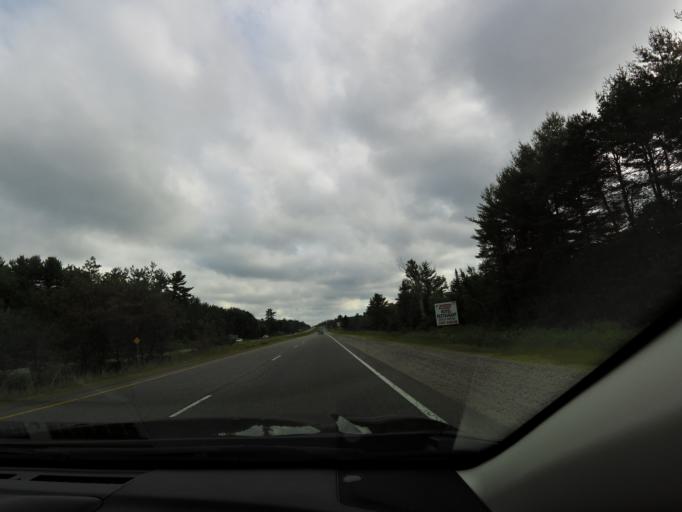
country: CA
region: Ontario
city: Gravenhurst
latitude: 44.9524
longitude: -79.3315
